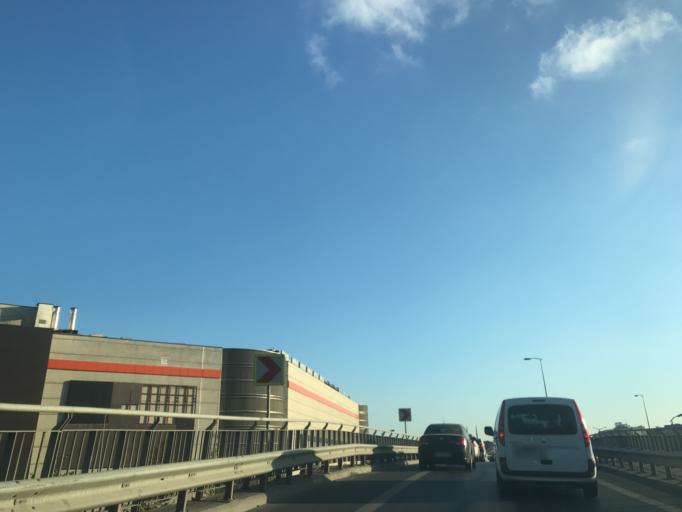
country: TR
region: Istanbul
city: Esenler
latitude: 41.0448
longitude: 28.8859
